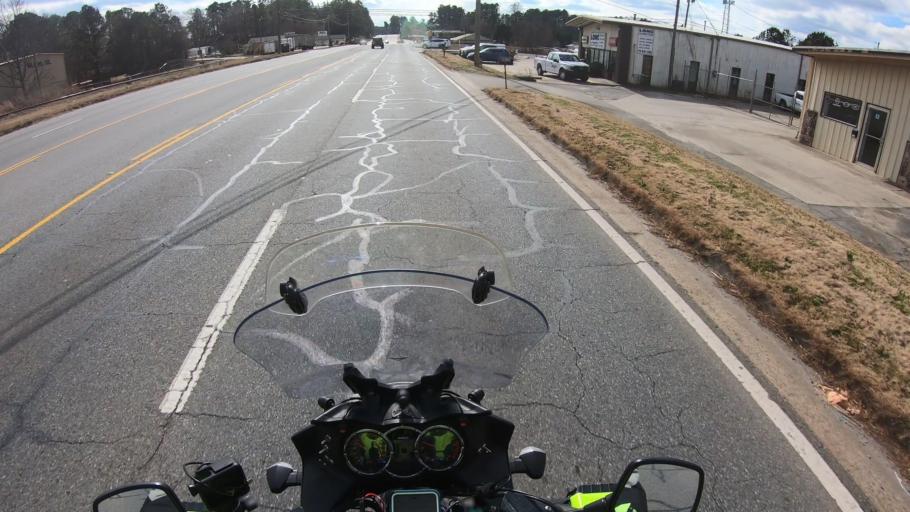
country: US
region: Georgia
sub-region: Cherokee County
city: Woodstock
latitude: 34.0632
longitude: -84.5197
